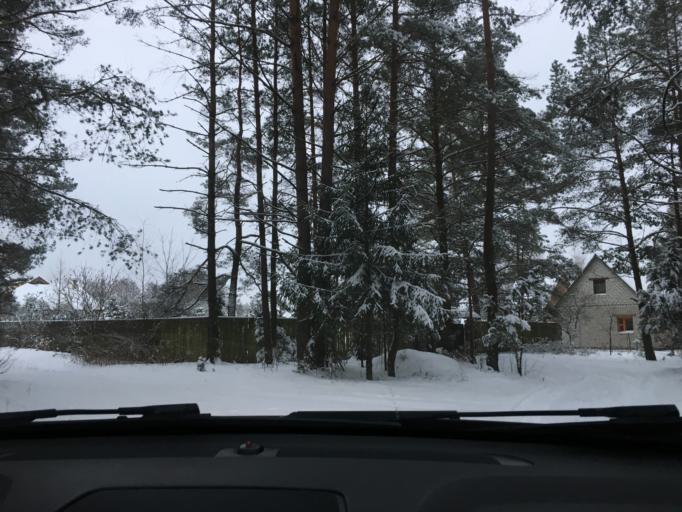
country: LT
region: Alytaus apskritis
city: Druskininkai
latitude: 53.9214
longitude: 24.1883
